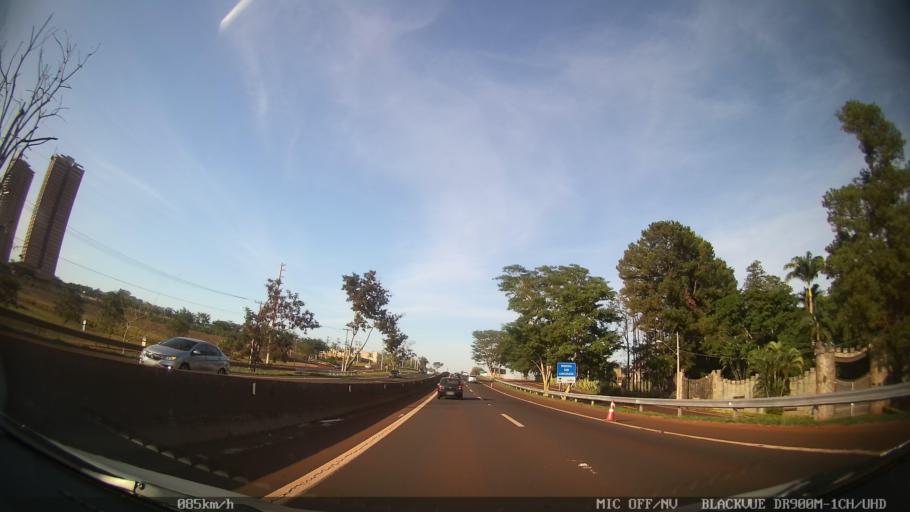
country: BR
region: Sao Paulo
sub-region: Ribeirao Preto
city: Ribeirao Preto
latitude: -21.2371
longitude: -47.8190
